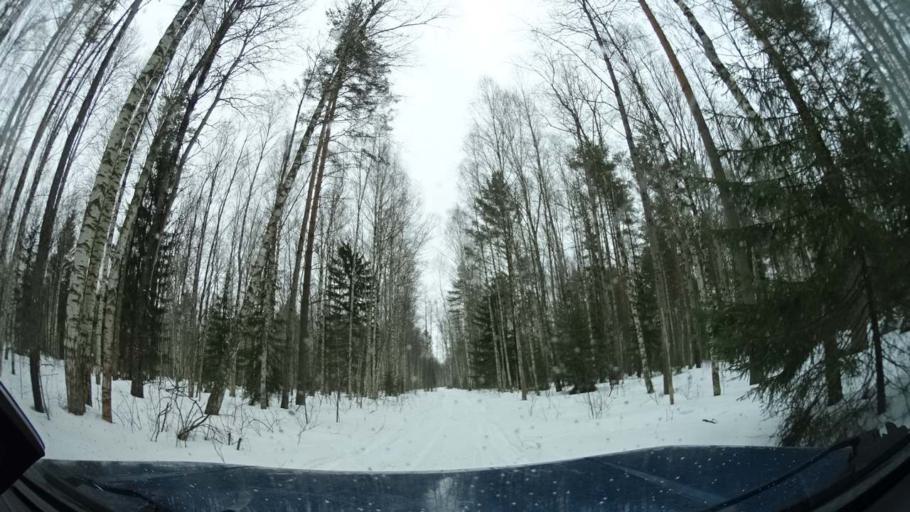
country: RU
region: Tverskaya
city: Gorodnya
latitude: 56.8109
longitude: 36.3808
